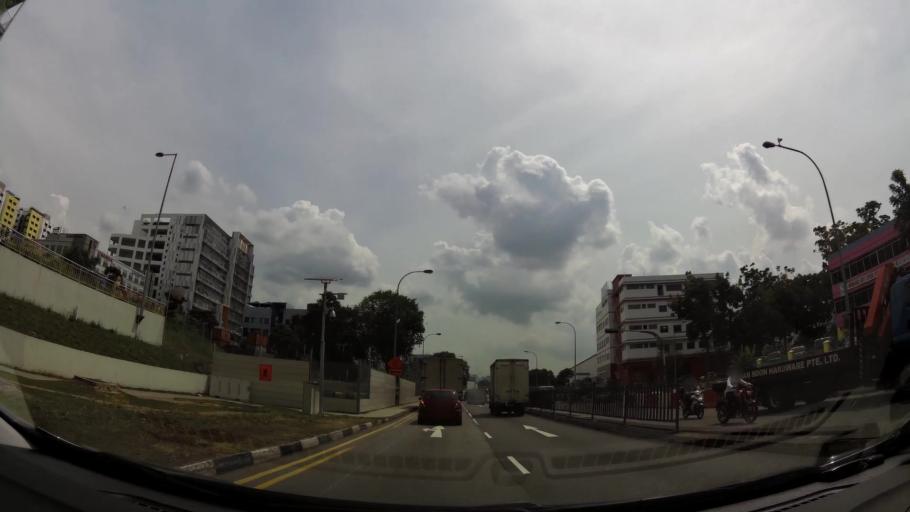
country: MY
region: Johor
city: Johor Bahru
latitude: 1.4081
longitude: 103.7561
